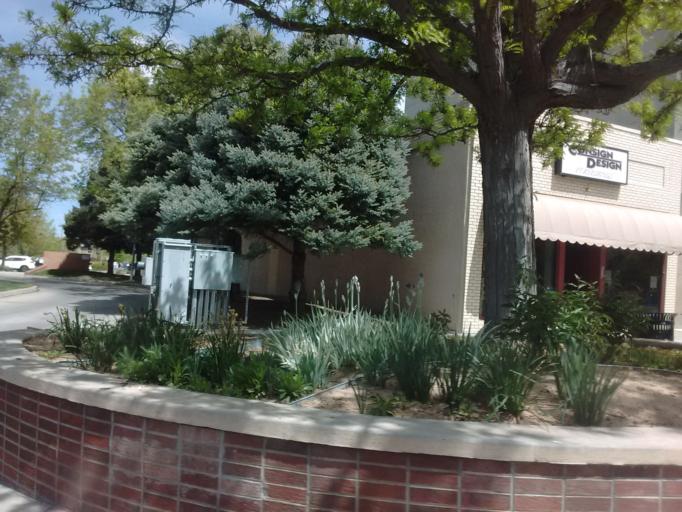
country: US
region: Colorado
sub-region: Mesa County
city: Grand Junction
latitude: 39.0673
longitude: -108.5688
